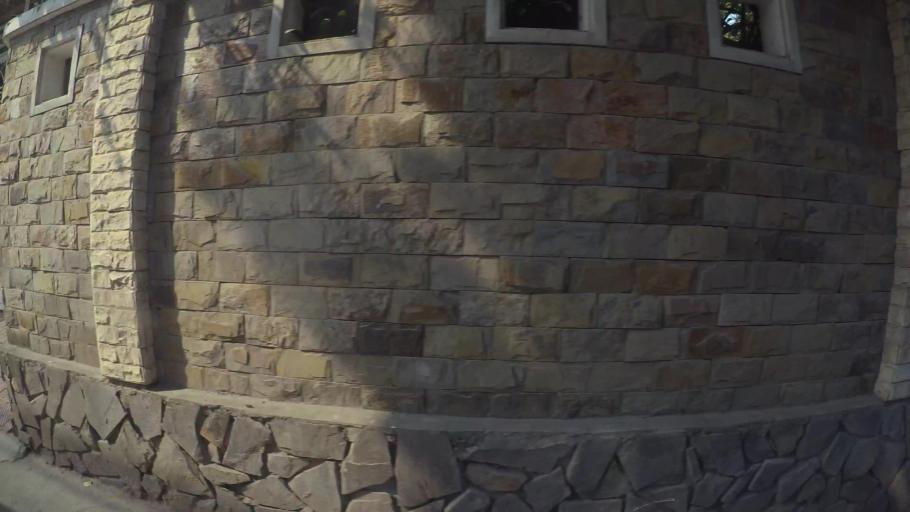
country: VN
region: Ha Noi
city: Ha Dong
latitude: 20.9992
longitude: 105.7526
